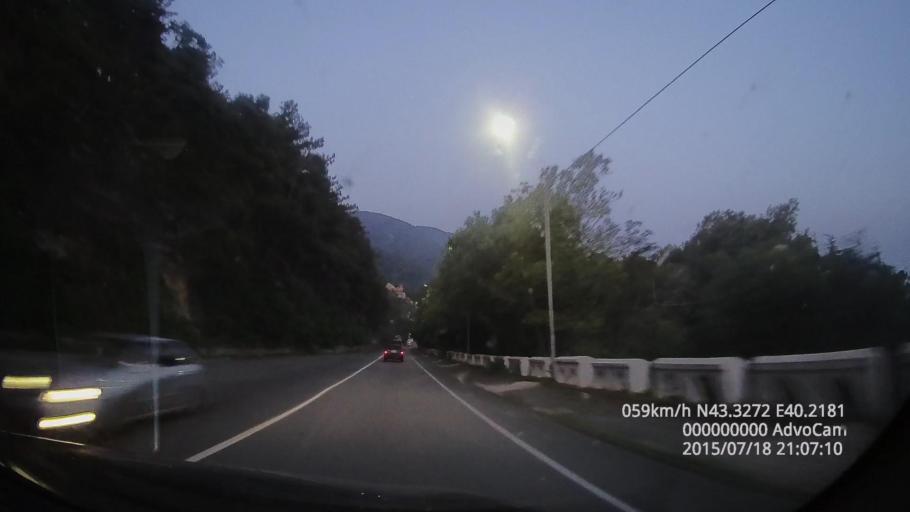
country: GE
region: Abkhazia
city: Gagra
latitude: 43.3272
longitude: 40.2185
